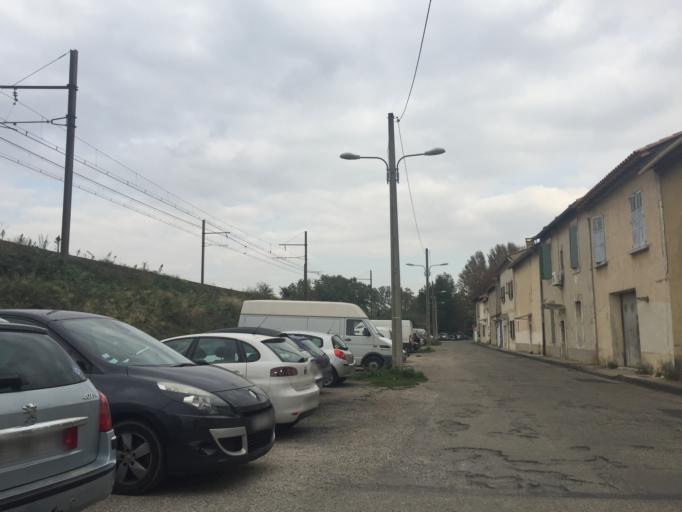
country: FR
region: Provence-Alpes-Cote d'Azur
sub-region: Departement du Vaucluse
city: Avignon
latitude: 43.9526
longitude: 4.8246
